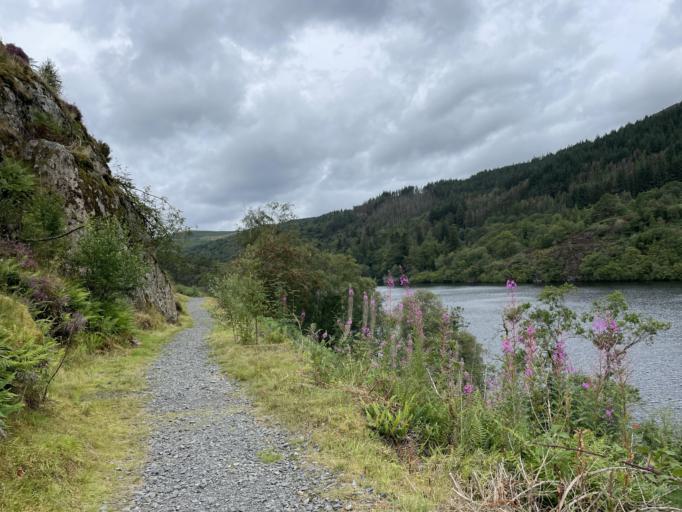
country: GB
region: Scotland
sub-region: Dumfries and Galloway
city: Newton Stewart
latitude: 55.0871
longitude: -4.4875
